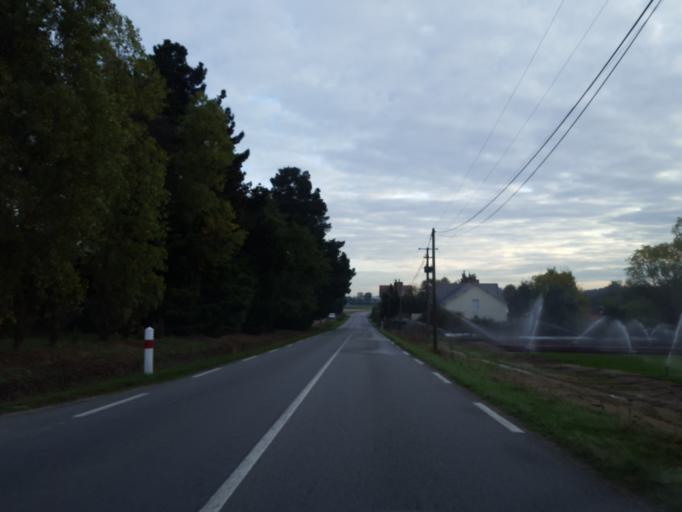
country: FR
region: Pays de la Loire
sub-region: Departement de la Loire-Atlantique
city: Saint-Julien-de-Concelles
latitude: 47.2318
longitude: -1.4034
